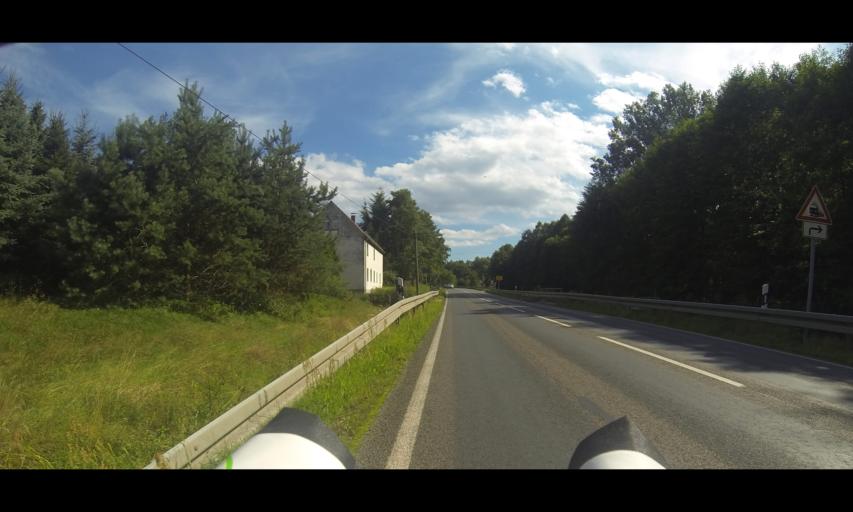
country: DE
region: Saxony
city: Ottendorf-Okrilla
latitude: 51.1598
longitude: 13.8072
